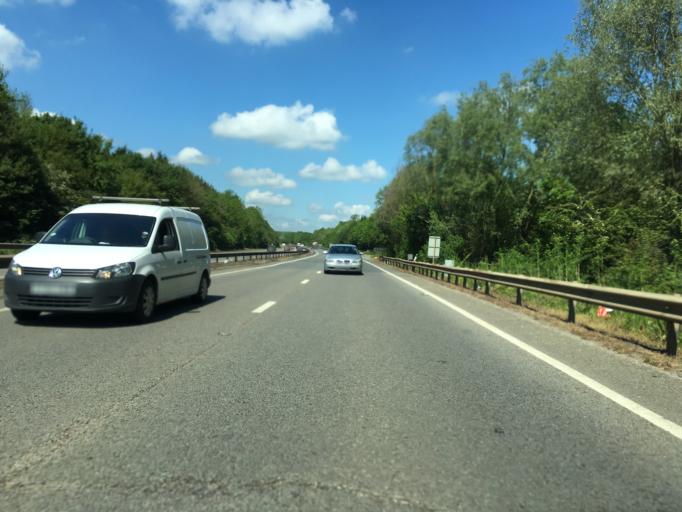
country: GB
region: England
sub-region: Milton Keynes
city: Bradwell
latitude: 52.0426
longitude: -0.7899
